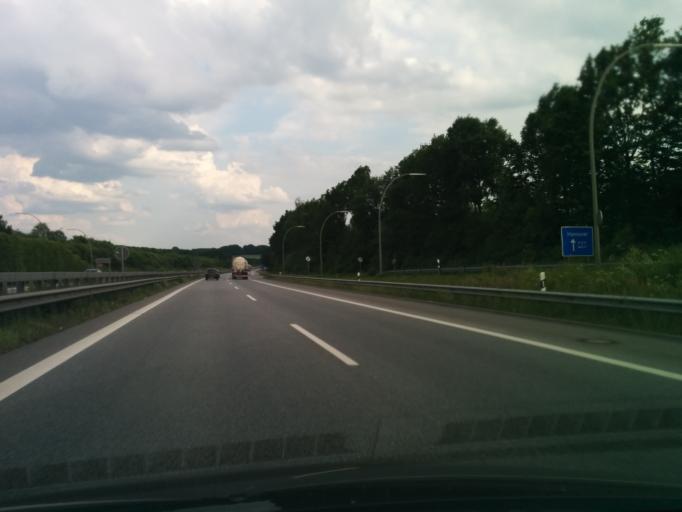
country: DE
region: Lower Saxony
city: Seevetal
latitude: 53.4236
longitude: 9.9657
